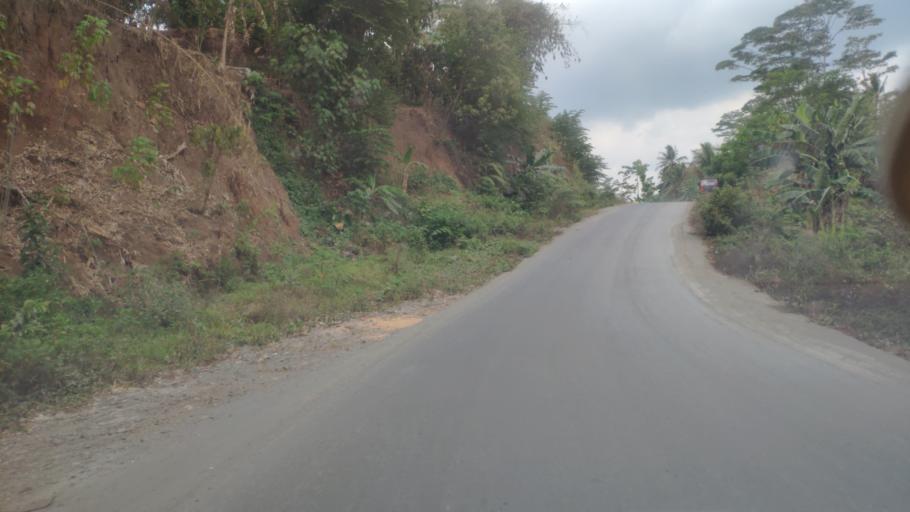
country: ID
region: Central Java
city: Wonosobo
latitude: -7.3847
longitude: 109.6637
